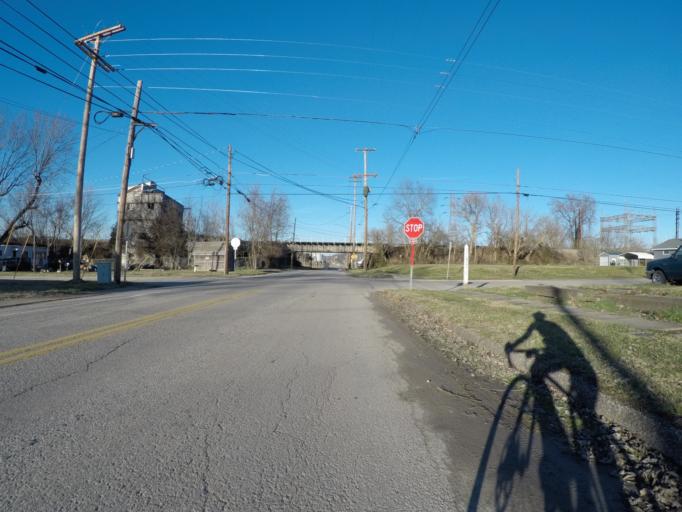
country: US
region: Kentucky
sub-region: Boyd County
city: Catlettsburg
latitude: 38.4013
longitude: -82.5920
